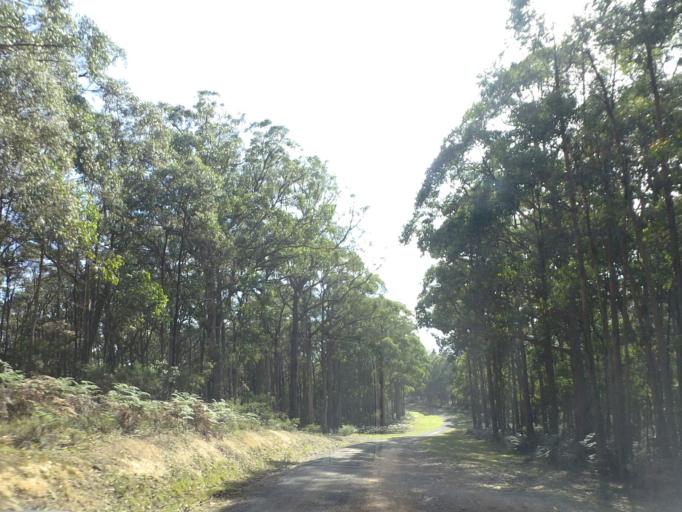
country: AU
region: Victoria
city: Brown Hill
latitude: -37.4462
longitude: 144.2044
